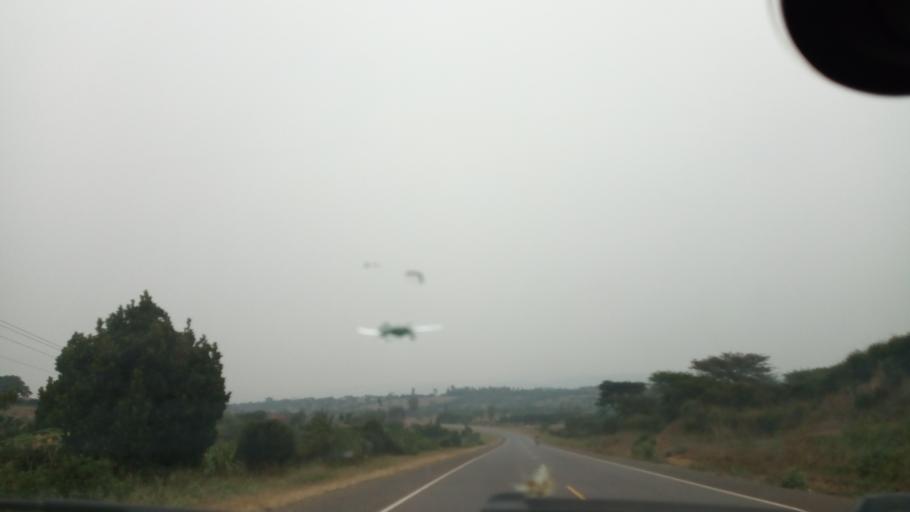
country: UG
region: Western Region
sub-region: Mbarara District
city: Mbarara
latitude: -0.7070
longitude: 30.7100
